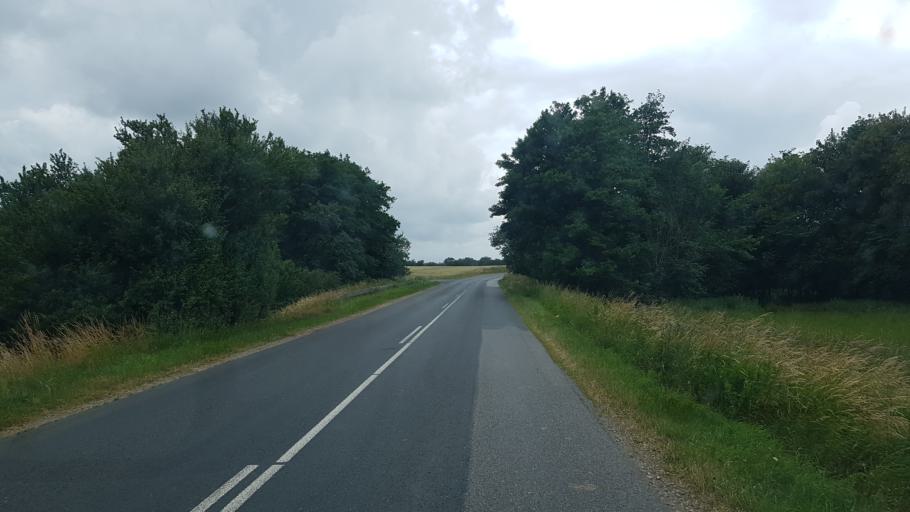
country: DK
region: South Denmark
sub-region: Kolding Kommune
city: Vamdrup
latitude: 55.4319
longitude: 9.2428
